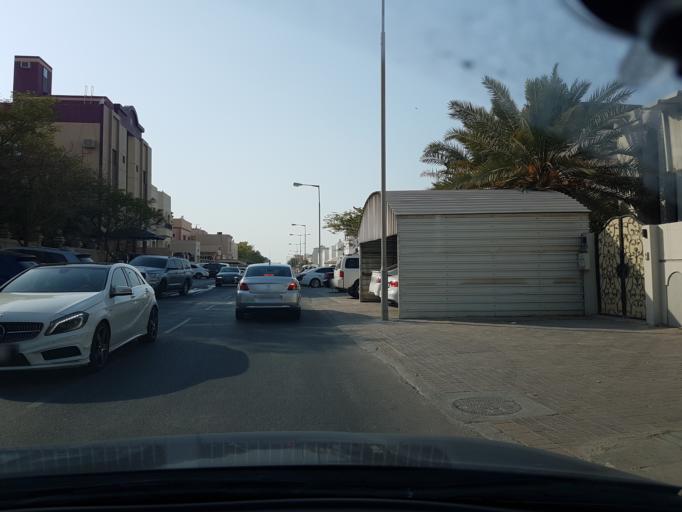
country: BH
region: Northern
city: Ar Rifa'
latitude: 26.1304
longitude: 50.5807
